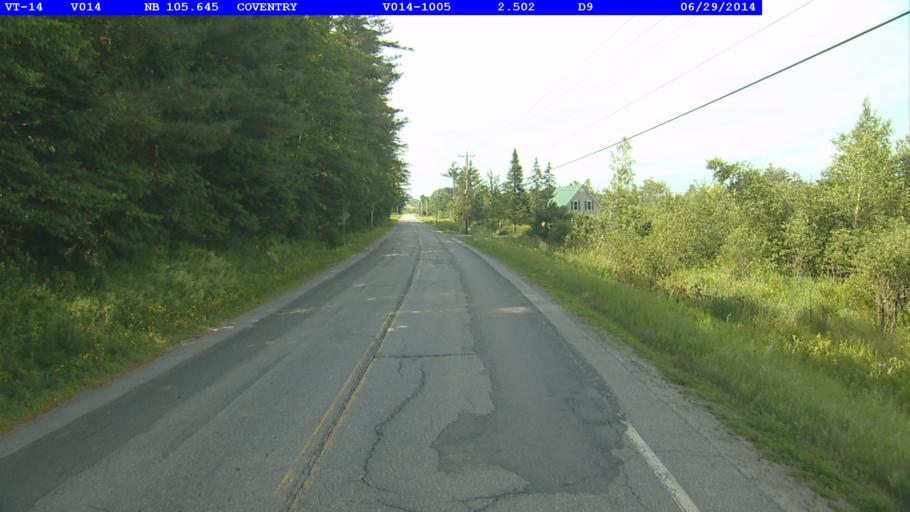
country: US
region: Vermont
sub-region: Orleans County
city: Newport
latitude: 44.8991
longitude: -72.2575
